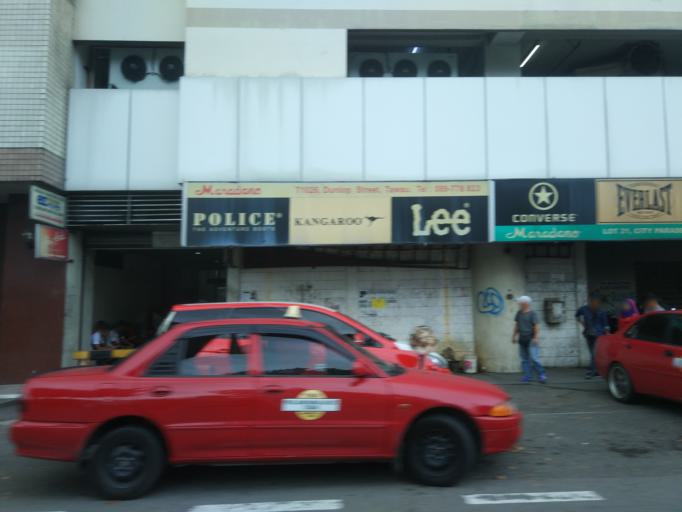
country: MY
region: Sabah
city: Kota Kinabalu
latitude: 5.9782
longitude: 116.0723
